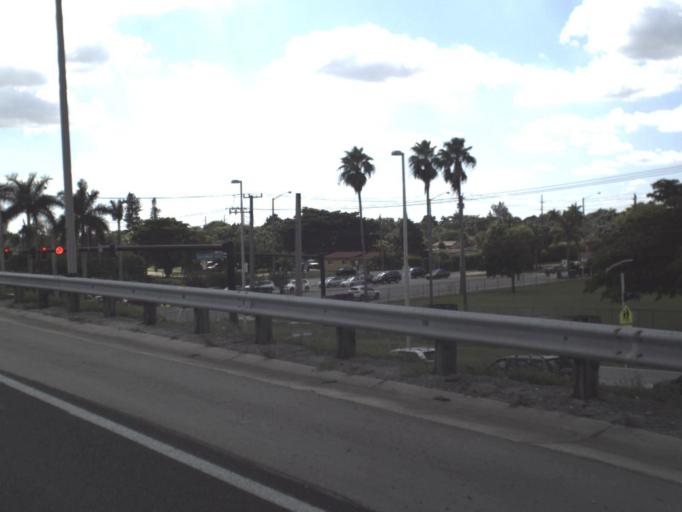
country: US
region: Florida
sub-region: Broward County
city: Pembroke Pines
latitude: 26.0109
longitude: -80.2131
